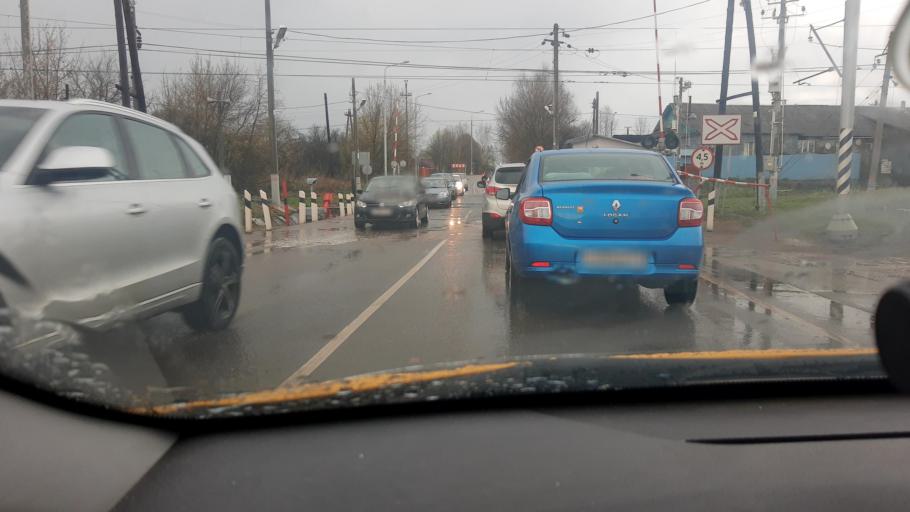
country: RU
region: Moskovskaya
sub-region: Volokolamskiy Rayon
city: Volokolamsk
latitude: 55.9946
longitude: 35.9221
